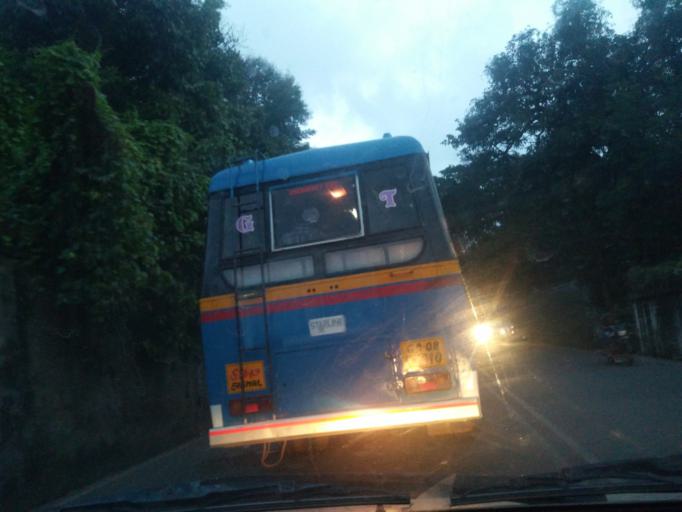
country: IN
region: Goa
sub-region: South Goa
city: Madgaon
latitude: 15.2810
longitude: 73.9603
